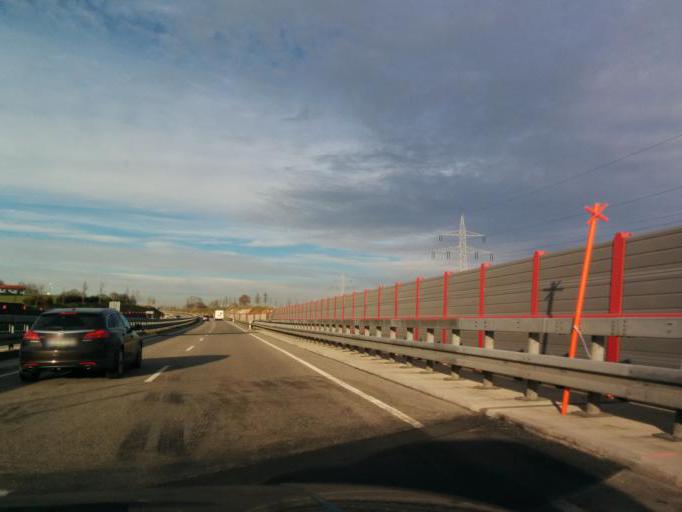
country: DE
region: Bavaria
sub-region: Swabia
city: Rettenberg
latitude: 47.6138
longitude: 10.2748
